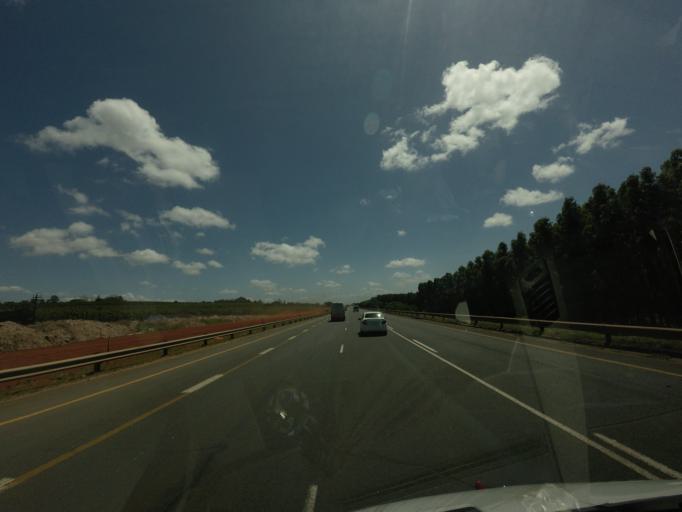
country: ZA
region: KwaZulu-Natal
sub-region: uThungulu District Municipality
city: Empangeni
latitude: -28.8108
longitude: 31.9154
